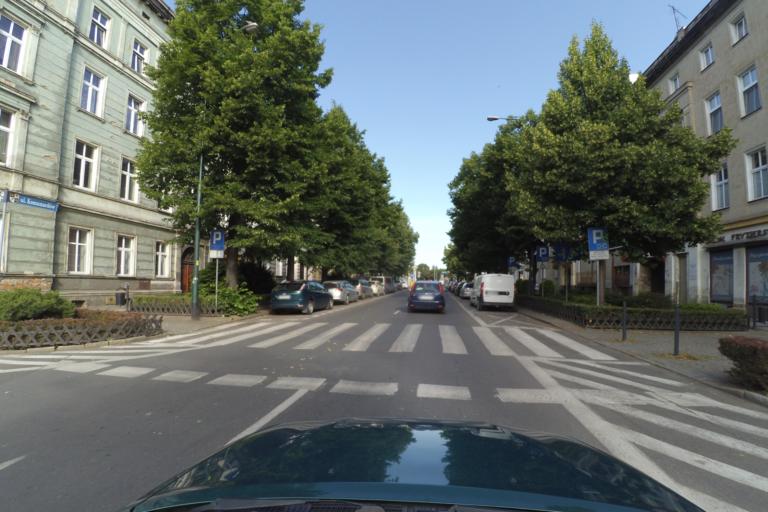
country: PL
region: Lower Silesian Voivodeship
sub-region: Powiat swidnicki
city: Swidnica
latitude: 50.8446
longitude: 16.4838
